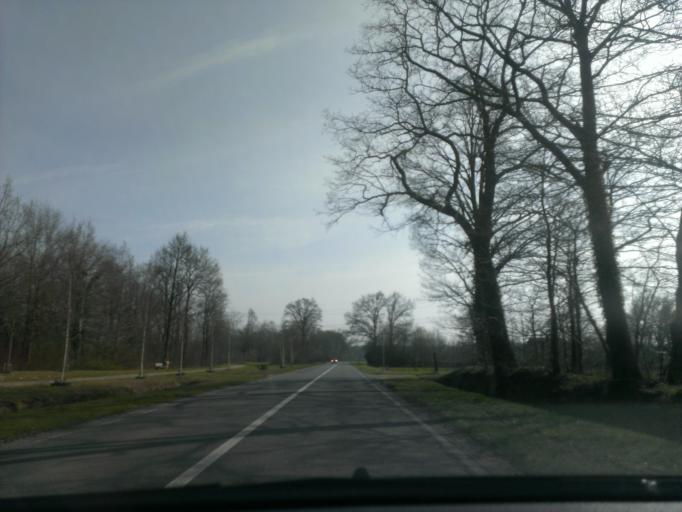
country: NL
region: Overijssel
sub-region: Gemeente Borne
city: Borne
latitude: 52.3002
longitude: 6.7291
